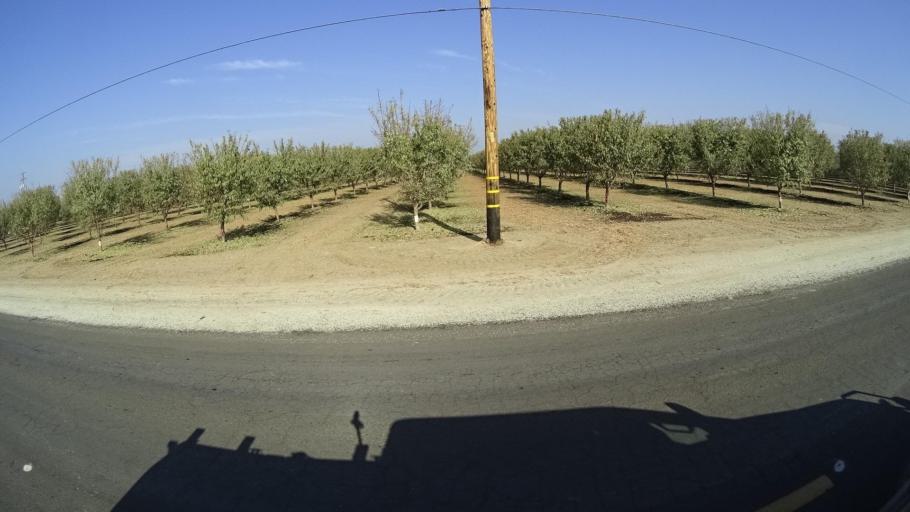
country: US
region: California
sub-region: Kern County
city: McFarland
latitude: 35.6891
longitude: -119.1995
